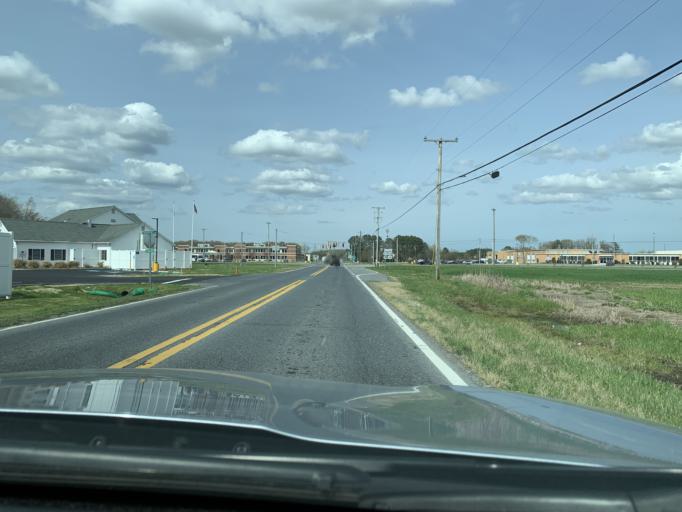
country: US
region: Delaware
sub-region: Sussex County
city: Georgetown
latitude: 38.6627
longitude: -75.3791
